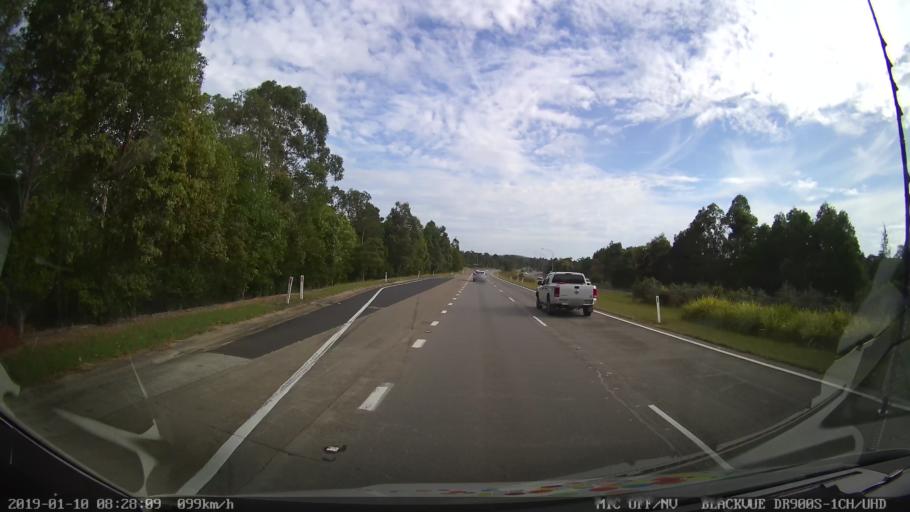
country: AU
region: New South Wales
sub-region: Coffs Harbour
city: Bonville
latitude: -30.3974
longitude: 153.0317
